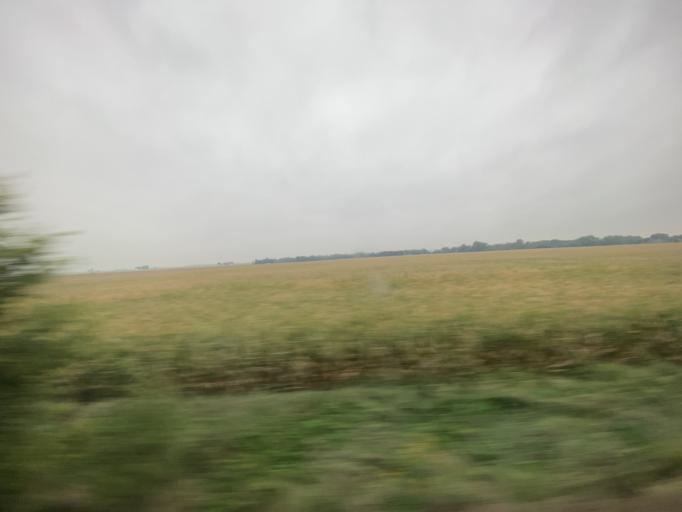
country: US
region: Illinois
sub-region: DeKalb County
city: Somonauk
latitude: 41.6209
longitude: -88.7575
